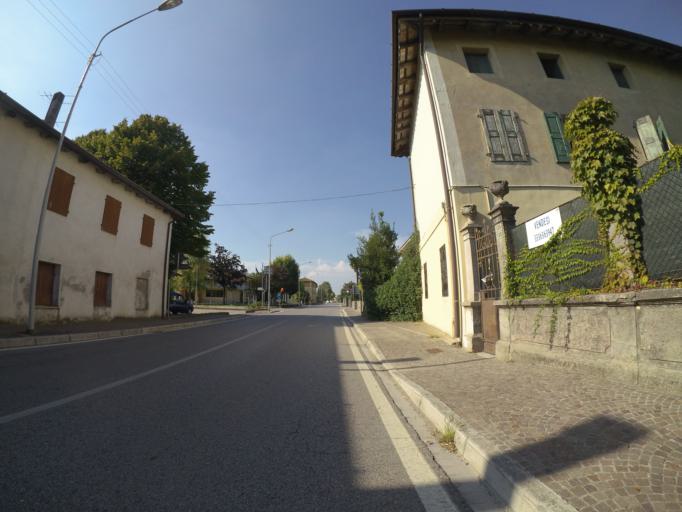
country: IT
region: Friuli Venezia Giulia
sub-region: Provincia di Udine
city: Pocenia
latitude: 45.8367
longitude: 13.0990
